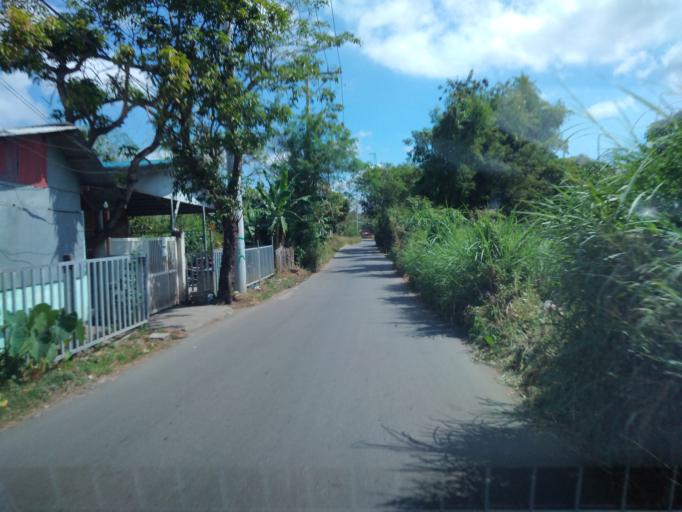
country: PH
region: Central Luzon
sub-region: Province of Bulacan
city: Guyong
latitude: 14.8473
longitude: 120.9916
